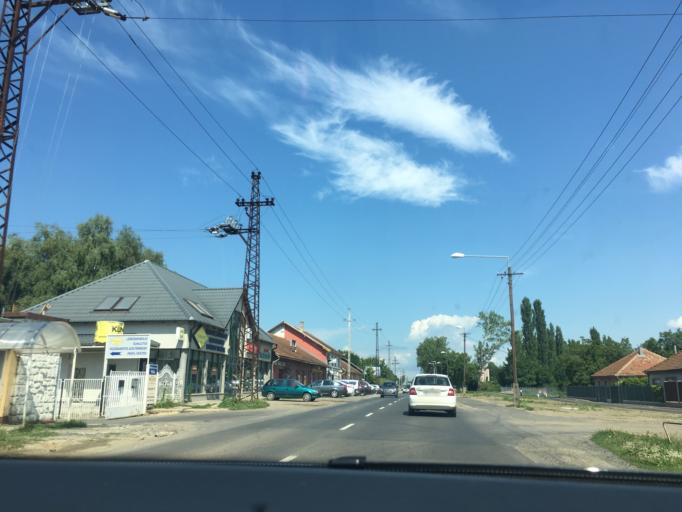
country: HU
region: Szabolcs-Szatmar-Bereg
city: Nyiregyhaza
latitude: 47.9639
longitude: 21.6998
